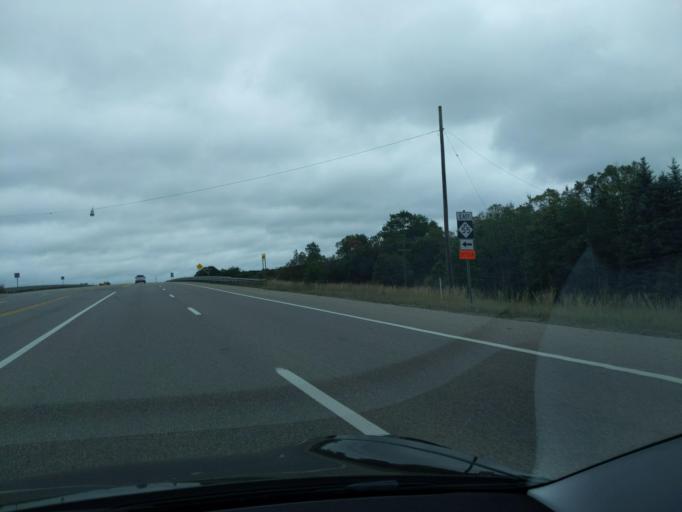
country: US
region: Michigan
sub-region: Wexford County
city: Cadillac
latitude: 44.2813
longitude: -85.3920
